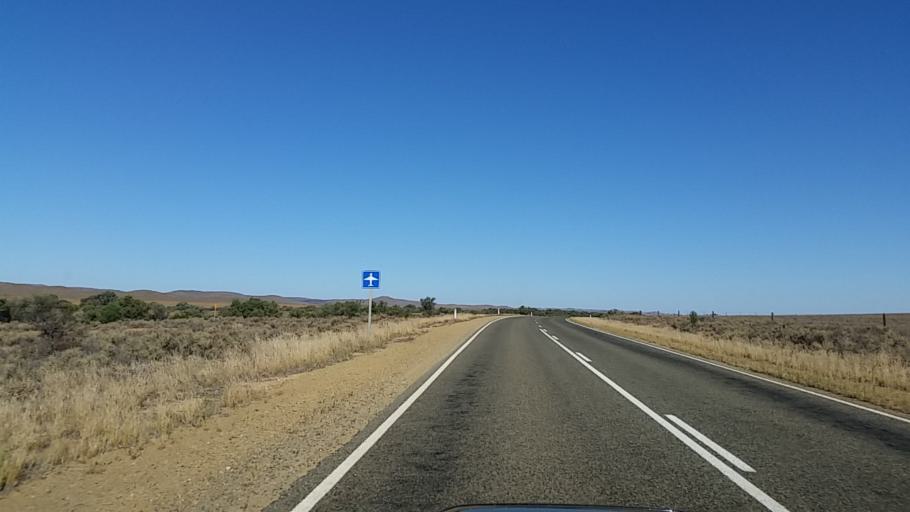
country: AU
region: South Australia
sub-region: Flinders Ranges
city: Quorn
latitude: -32.4014
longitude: 138.5151
